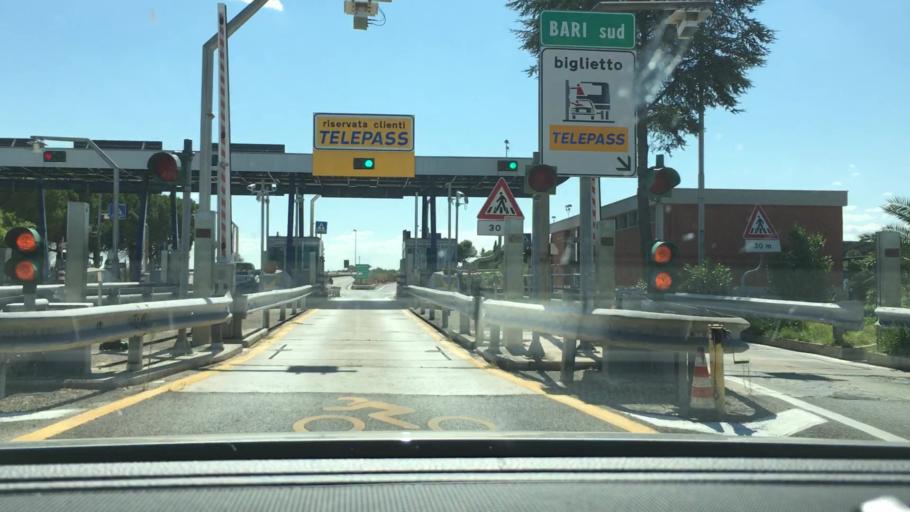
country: IT
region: Apulia
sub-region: Provincia di Bari
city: Bitritto
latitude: 41.0687
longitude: 16.8313
